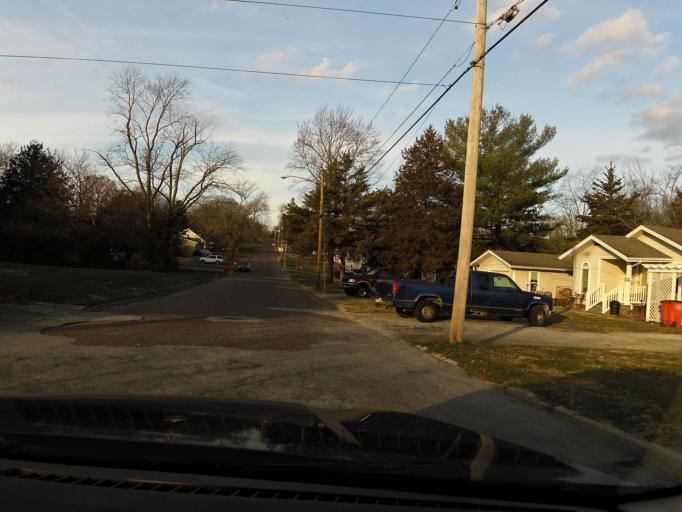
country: US
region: Illinois
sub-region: Fayette County
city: Vandalia
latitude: 38.9608
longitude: -89.1016
